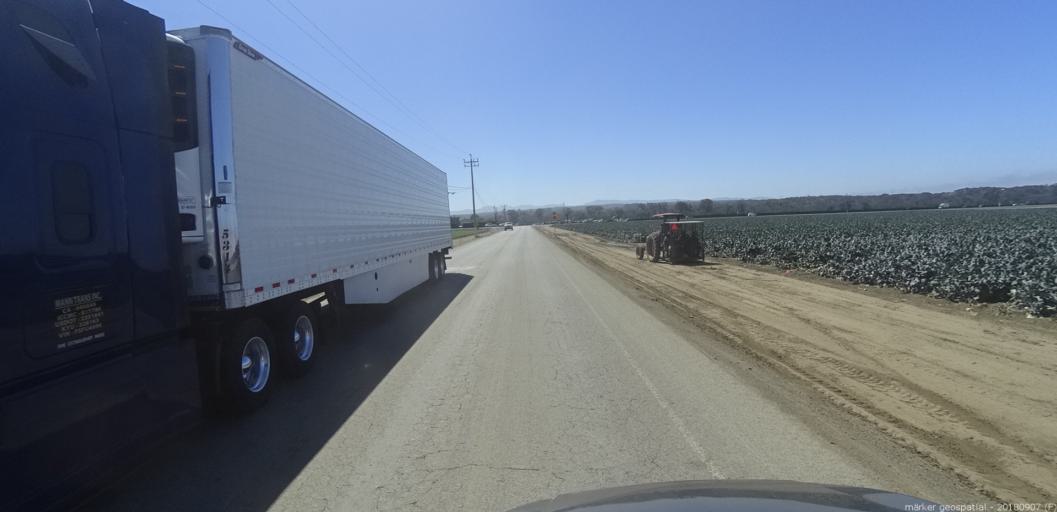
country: US
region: California
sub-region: Monterey County
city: Boronda
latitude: 36.6812
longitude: -121.7351
